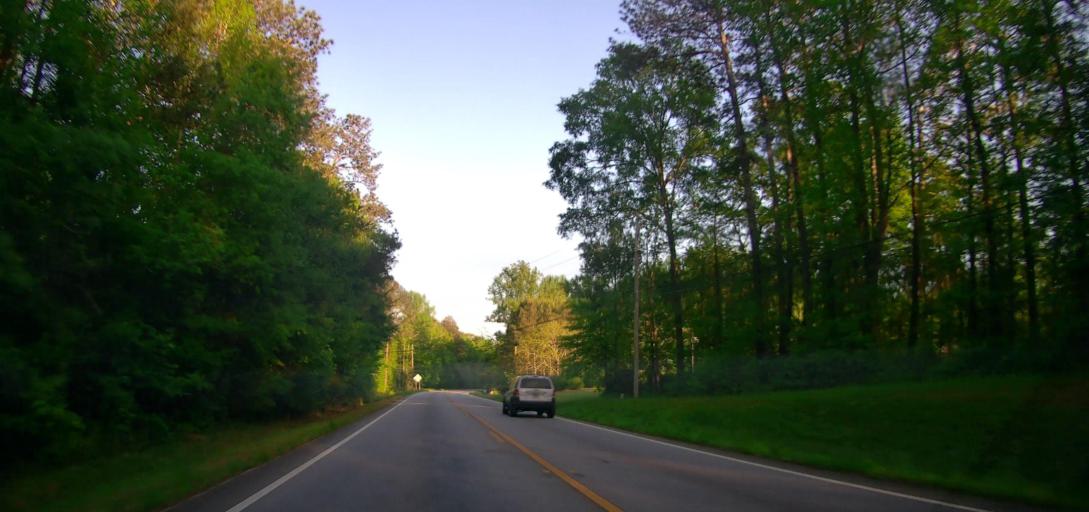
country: US
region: Georgia
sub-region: Newton County
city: Covington
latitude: 33.5880
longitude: -83.7871
